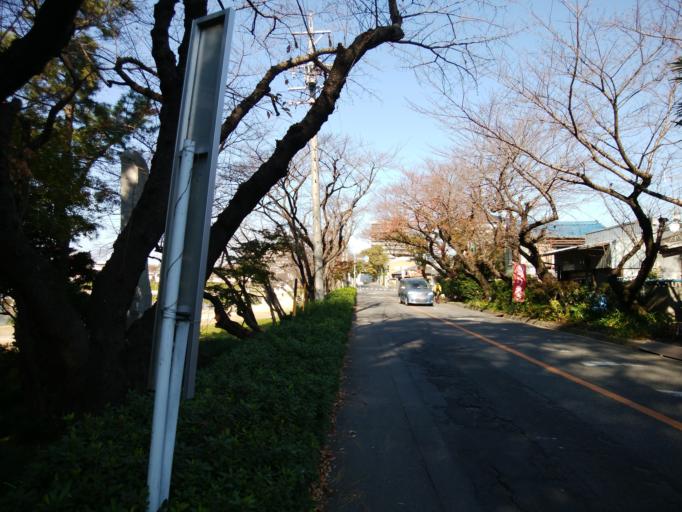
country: JP
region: Aichi
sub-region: Tsushima-shi
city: Tsushima
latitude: 35.1753
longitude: 136.7229
